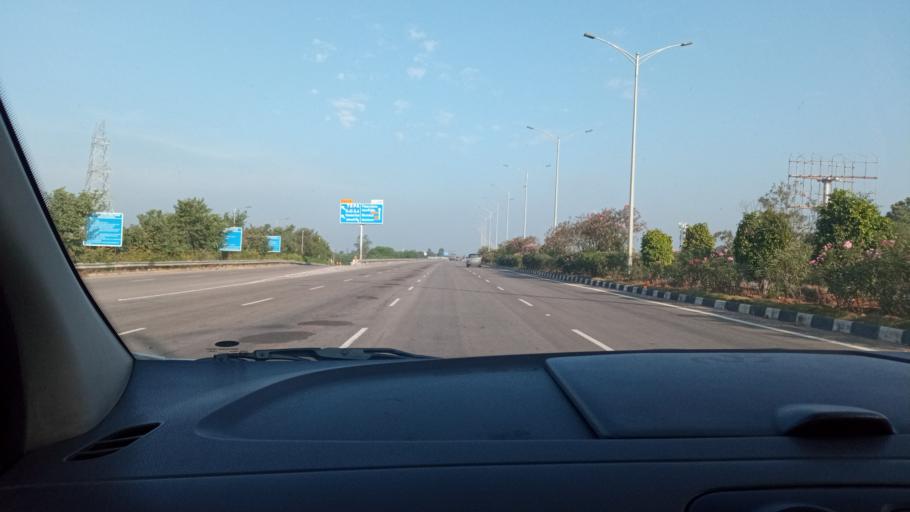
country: IN
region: Telangana
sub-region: Hyderabad
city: Hyderabad
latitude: 17.3452
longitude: 78.3624
